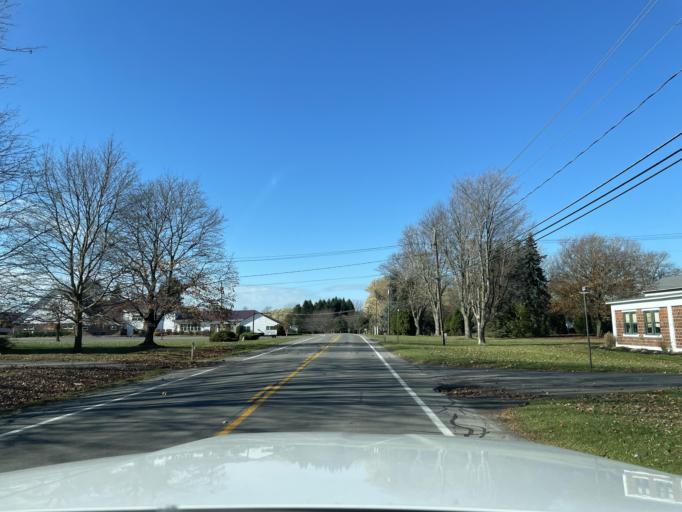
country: US
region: New York
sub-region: Orleans County
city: Medina
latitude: 43.2211
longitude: -78.4108
